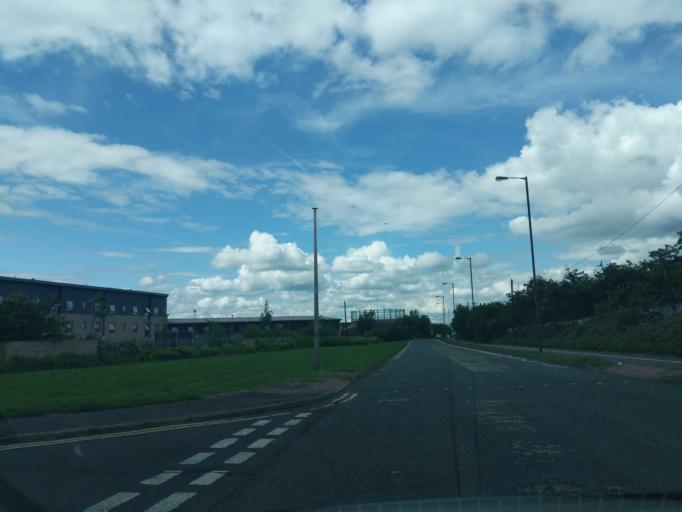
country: GB
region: Scotland
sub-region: Edinburgh
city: Edinburgh
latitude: 55.9737
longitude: -3.2407
